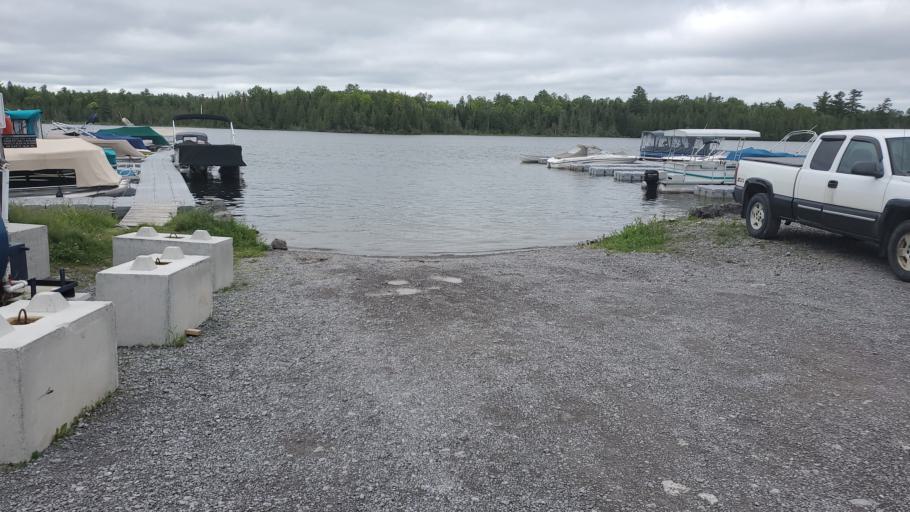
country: CA
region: Ontario
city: Arnprior
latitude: 45.3242
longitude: -76.4874
